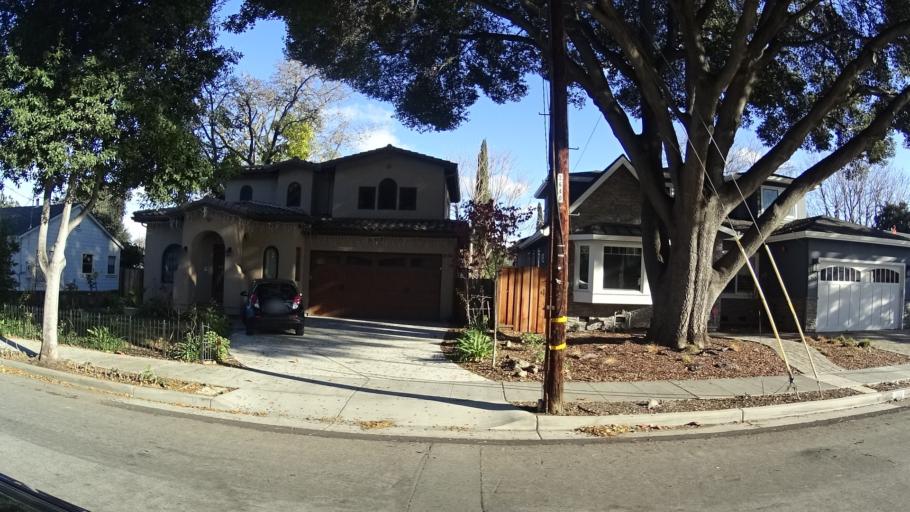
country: US
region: California
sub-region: Santa Clara County
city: Sunnyvale
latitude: 37.3768
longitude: -122.0388
